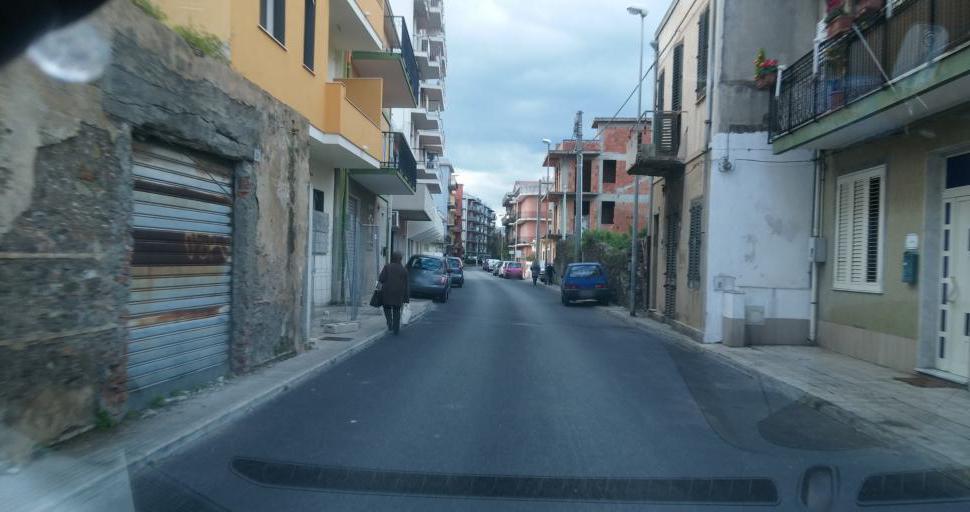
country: IT
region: Sicily
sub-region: Messina
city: Milazzo
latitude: 38.2187
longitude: 15.2360
